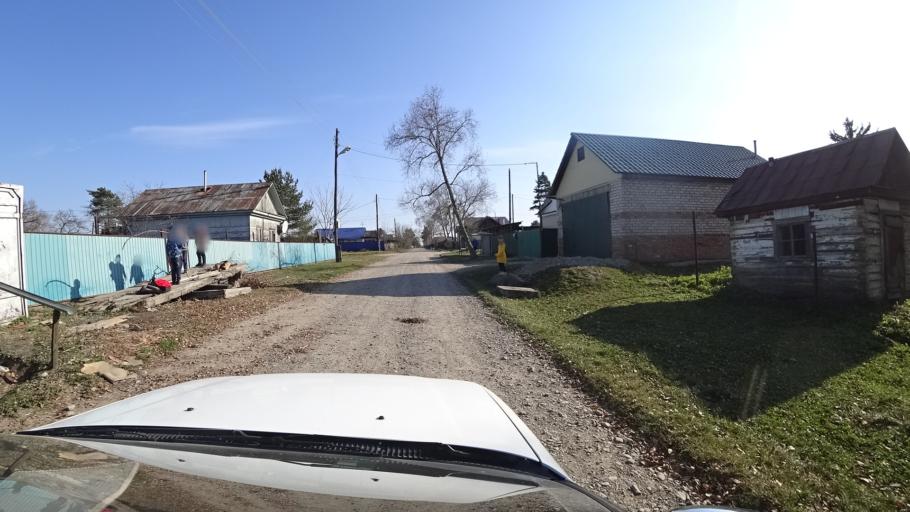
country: RU
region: Primorskiy
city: Dal'nerechensk
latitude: 45.9230
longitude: 133.7334
